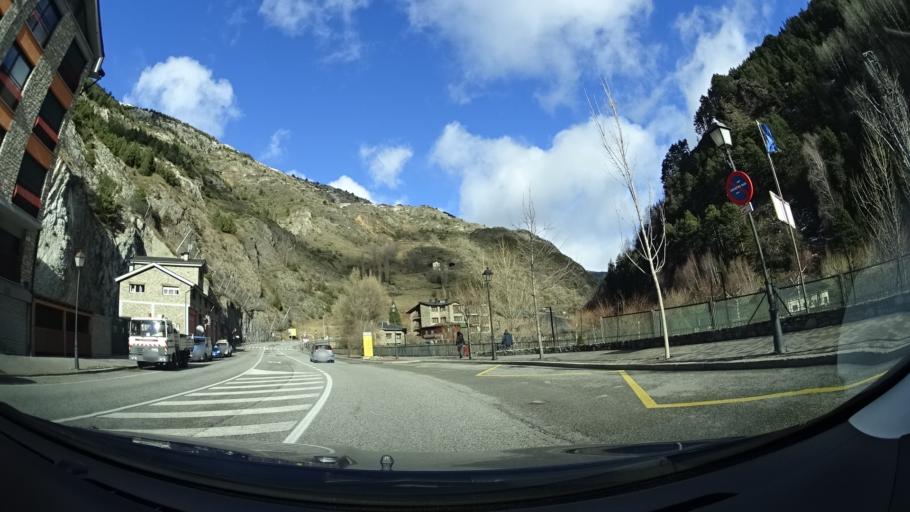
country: AD
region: Canillo
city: Canillo
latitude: 42.5689
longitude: 1.6043
